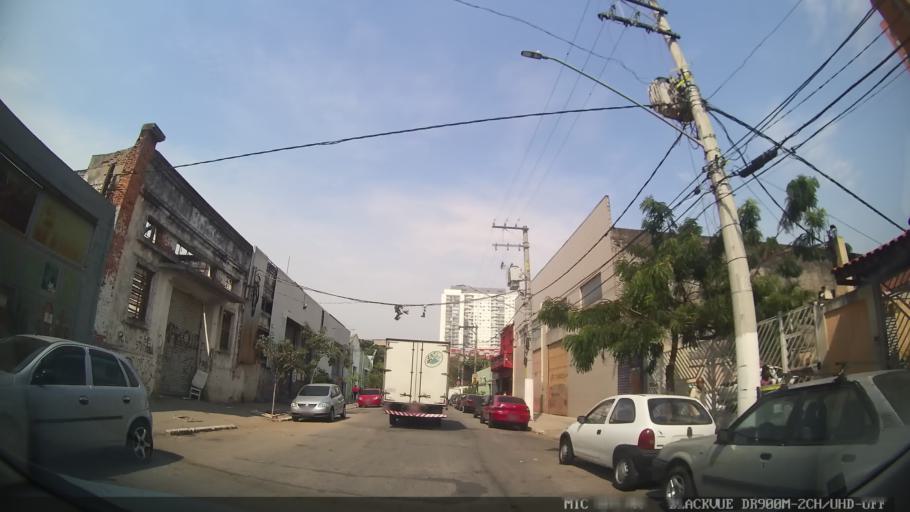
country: BR
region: Sao Paulo
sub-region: Sao Paulo
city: Sao Paulo
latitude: -23.5465
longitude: -46.6174
